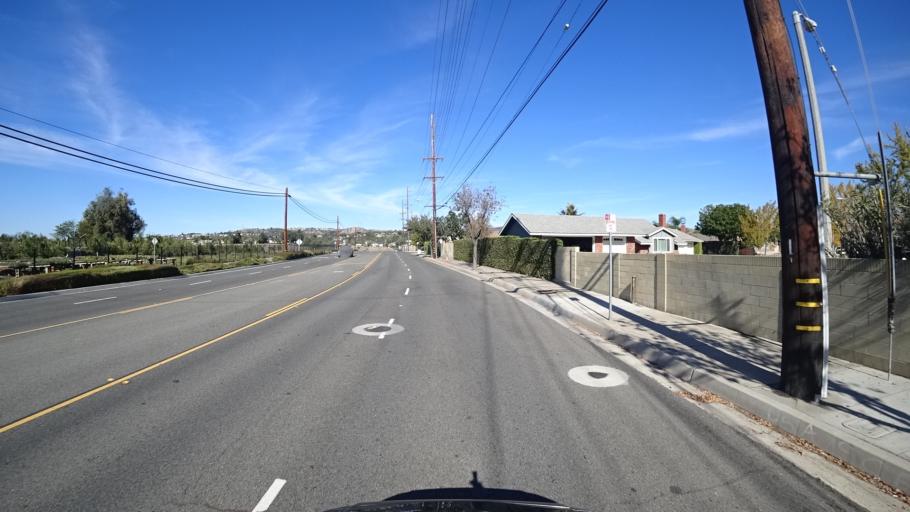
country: US
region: California
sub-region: Orange County
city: Villa Park
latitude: 33.8074
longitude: -117.8009
